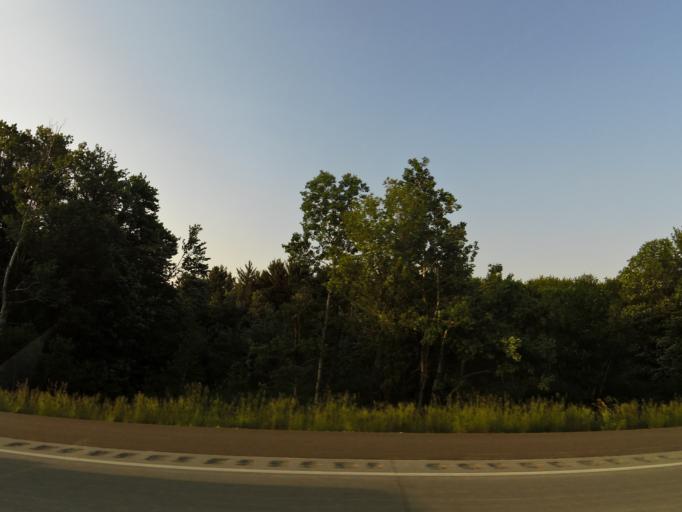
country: US
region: Wisconsin
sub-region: Jackson County
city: Black River Falls
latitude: 44.3520
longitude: -90.9432
